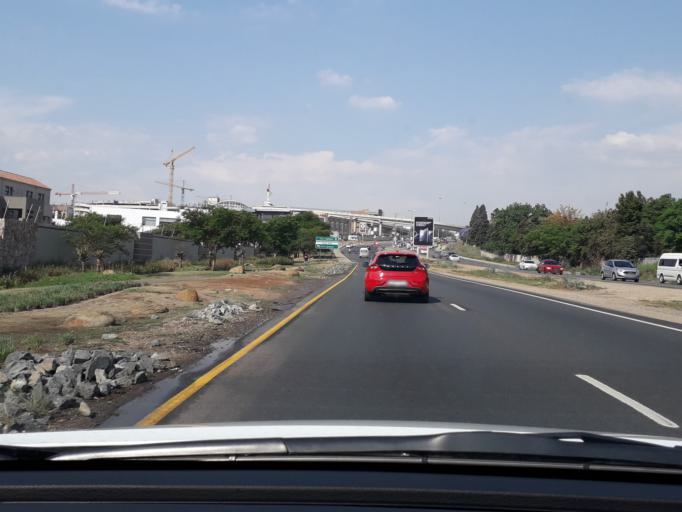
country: ZA
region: Gauteng
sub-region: City of Johannesburg Metropolitan Municipality
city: Diepsloot
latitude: -26.0224
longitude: 27.9998
